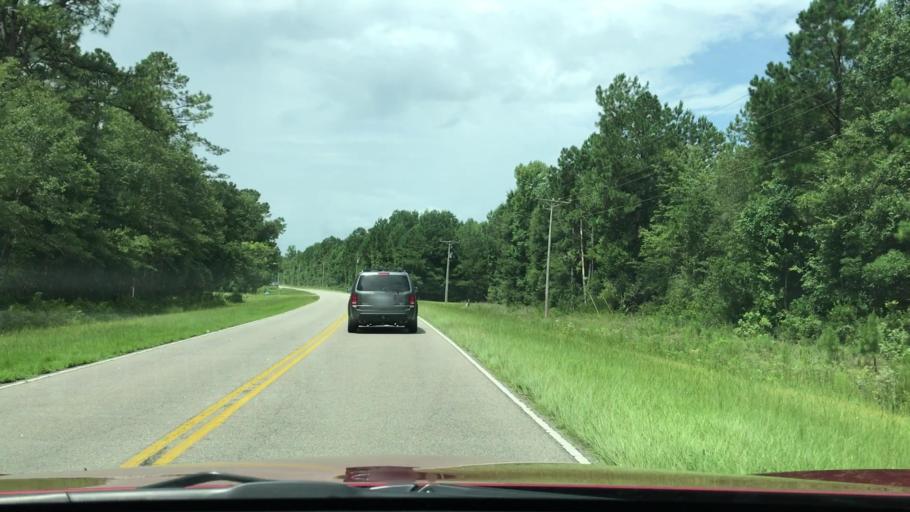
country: US
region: South Carolina
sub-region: Horry County
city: Red Hill
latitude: 33.9037
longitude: -78.9124
